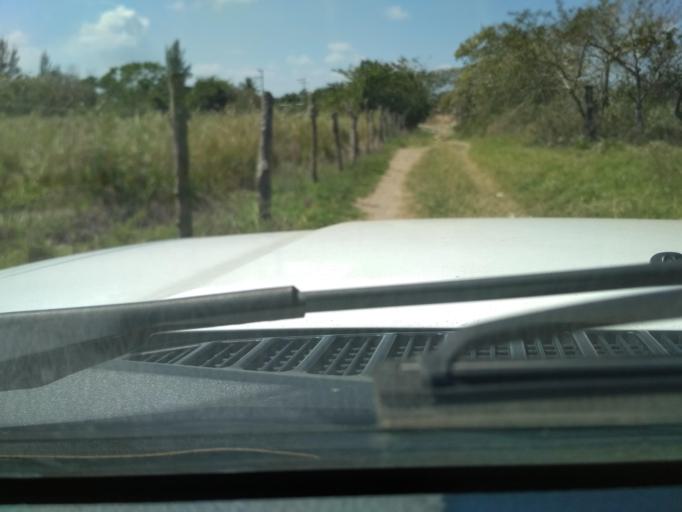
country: MX
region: Veracruz
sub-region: Veracruz
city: Las Amapolas
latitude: 19.1379
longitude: -96.2257
